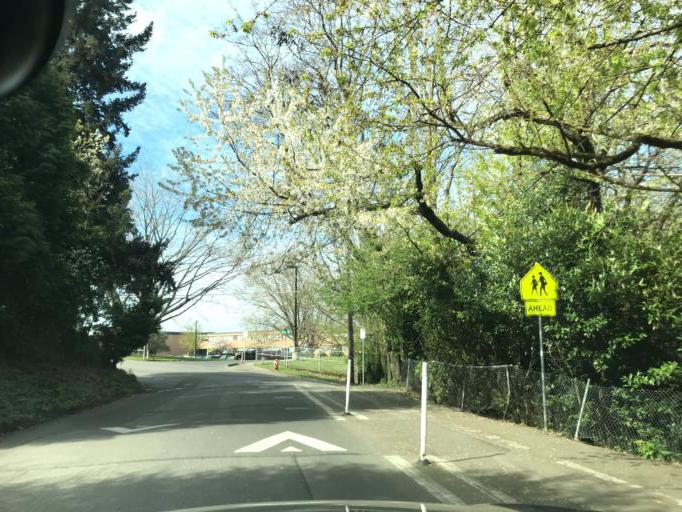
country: US
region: Oregon
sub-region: Multnomah County
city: Lents
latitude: 45.4953
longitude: -122.5695
